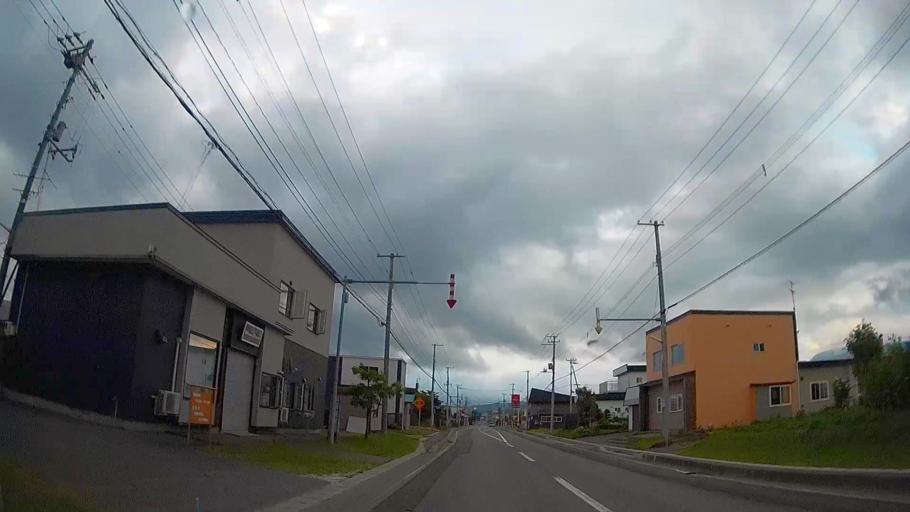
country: JP
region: Hokkaido
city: Nanae
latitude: 42.0442
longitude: 140.8116
